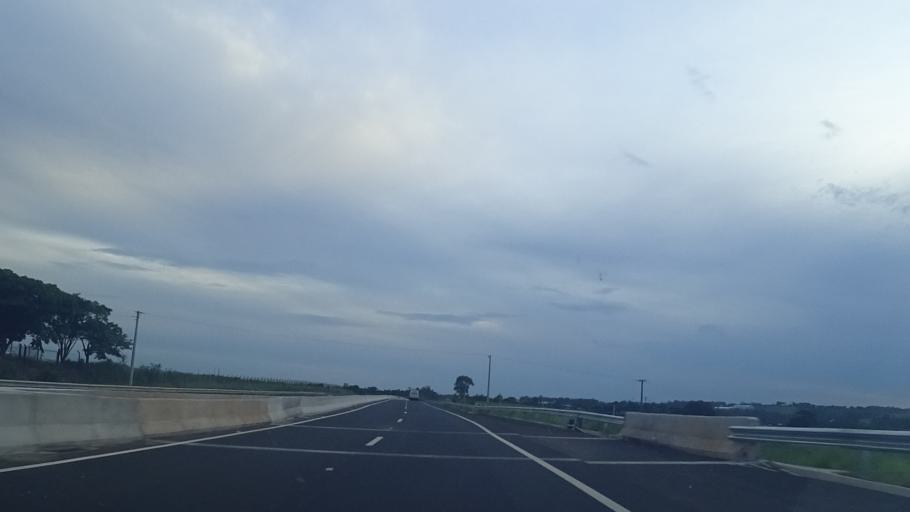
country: BR
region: Sao Paulo
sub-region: Presidente Prudente
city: Presidente Prudente
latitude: -22.1795
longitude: -51.4166
